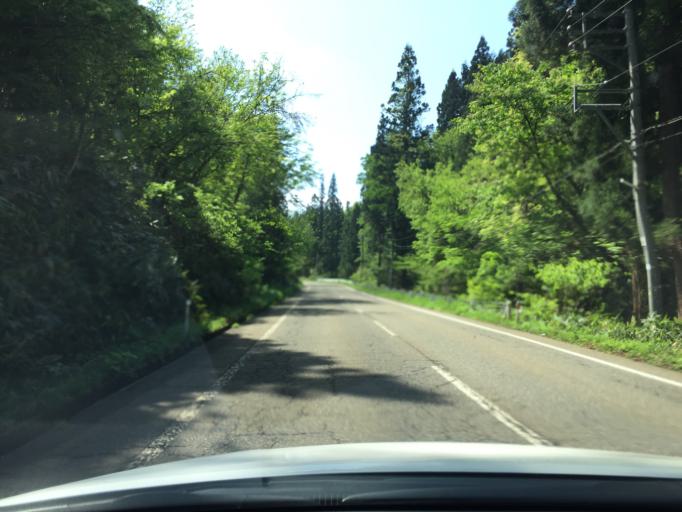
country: JP
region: Niigata
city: Tochio-honcho
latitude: 37.5335
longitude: 139.0923
